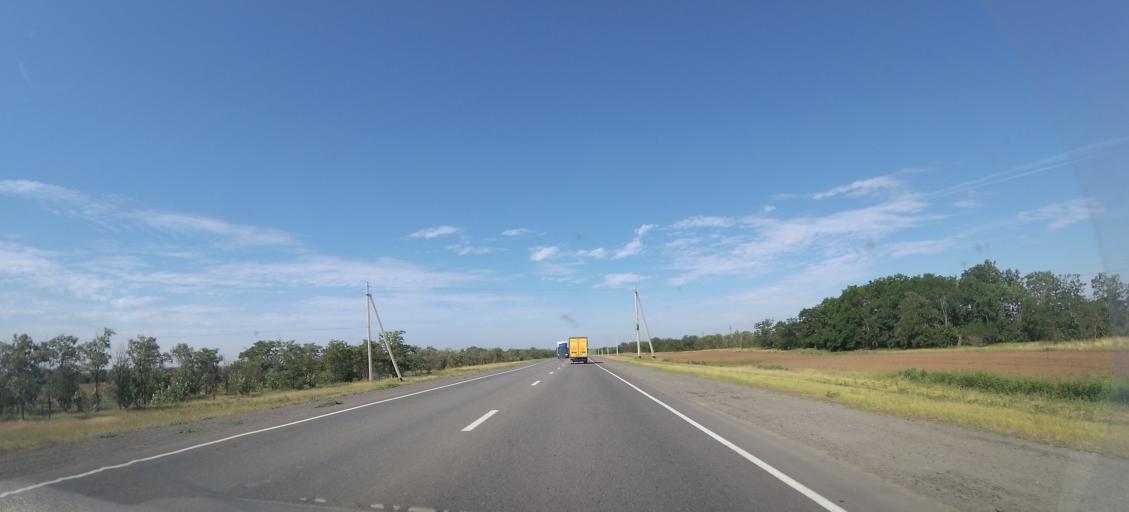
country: RU
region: Volgograd
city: Oktyabr'skiy
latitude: 48.6934
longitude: 43.7856
